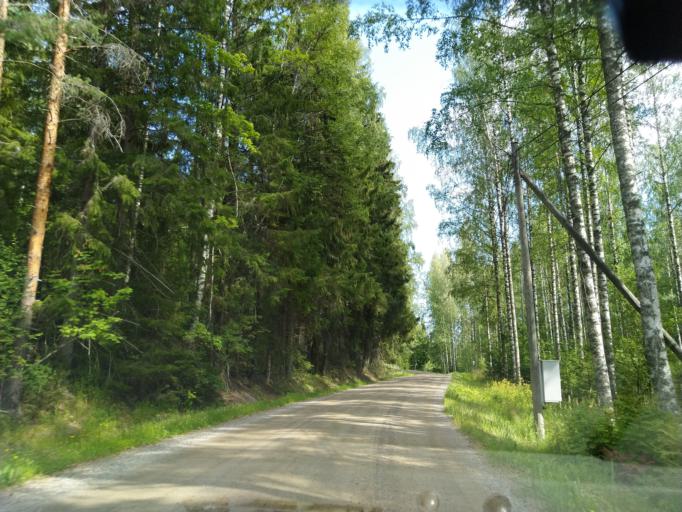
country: FI
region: Pirkanmaa
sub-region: Ylae-Pirkanmaa
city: Ruovesi
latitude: 61.9579
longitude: 24.0261
